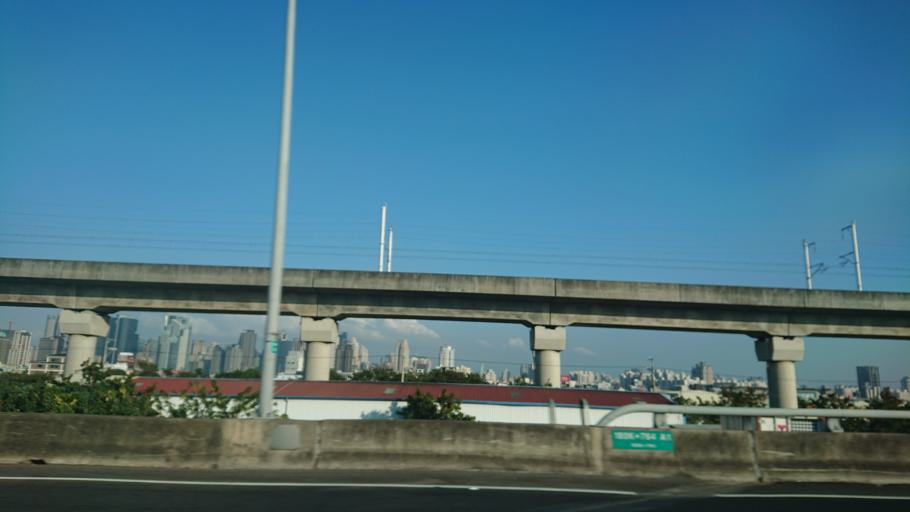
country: TW
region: Taiwan
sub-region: Taichung City
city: Taichung
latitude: 24.1587
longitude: 120.6206
